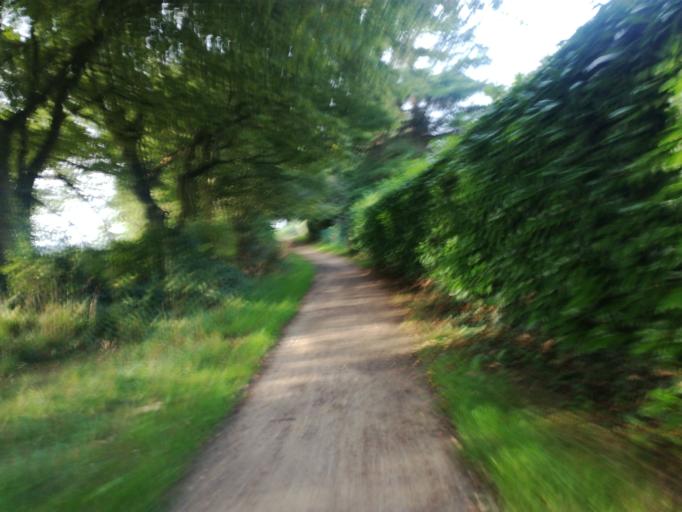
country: FR
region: Brittany
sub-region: Departement d'Ille-et-Vilaine
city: Cesson-Sevigne
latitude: 48.1317
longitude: -1.5907
